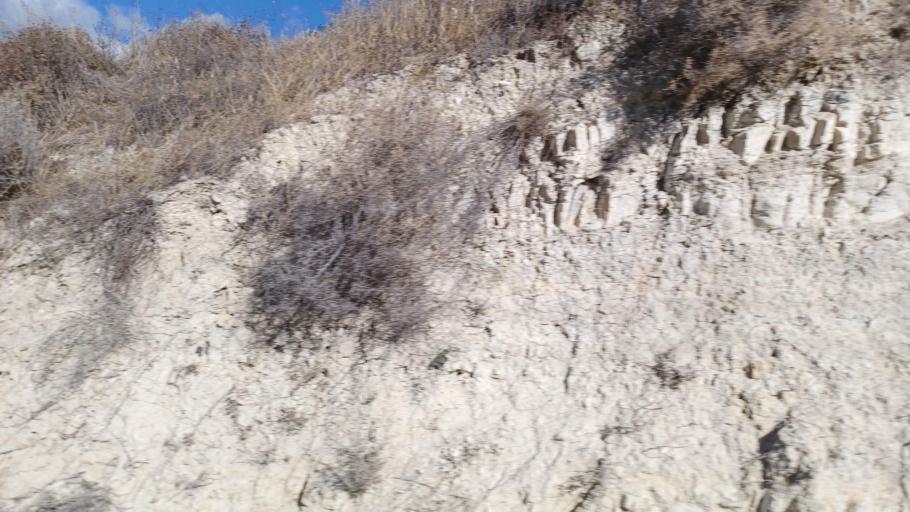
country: CY
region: Limassol
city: Pano Polemidia
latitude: 34.7439
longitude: 32.9863
